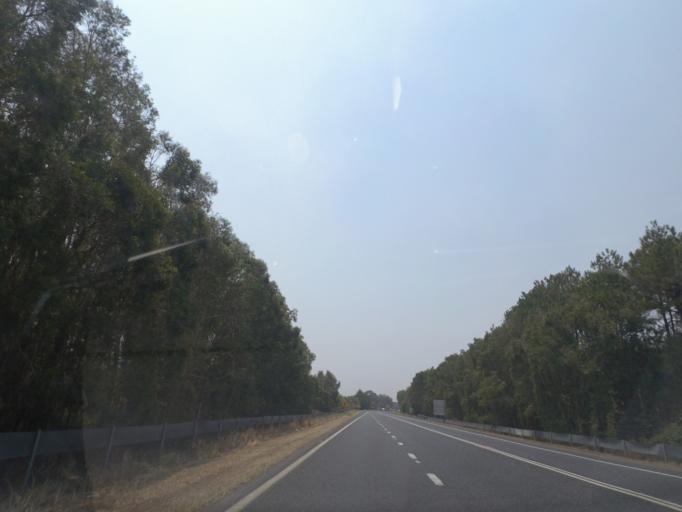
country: AU
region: New South Wales
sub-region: Ballina
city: Ballina
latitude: -28.9382
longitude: 153.4704
